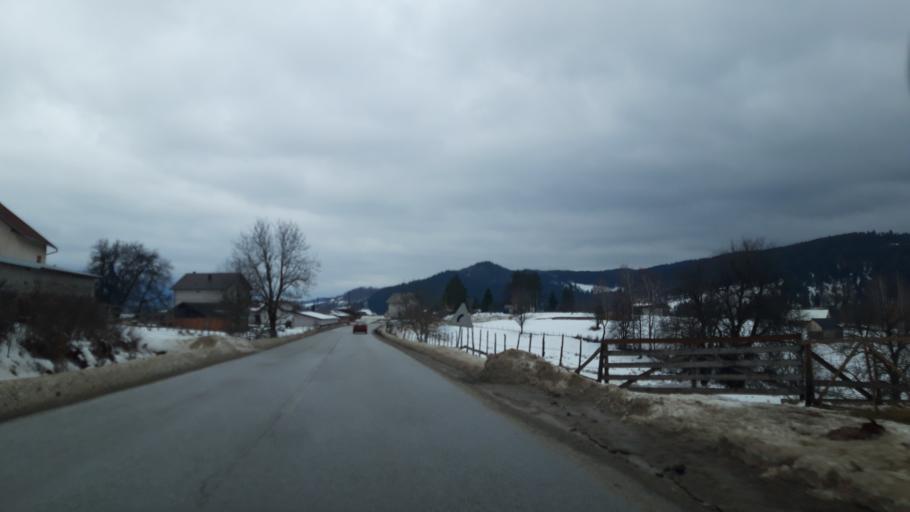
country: BA
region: Republika Srpska
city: Pale
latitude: 43.8922
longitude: 18.6288
